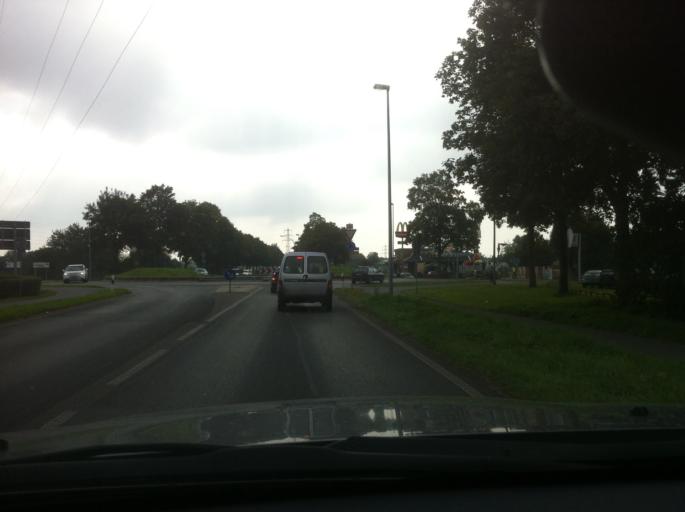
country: DE
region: North Rhine-Westphalia
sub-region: Regierungsbezirk Dusseldorf
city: Kleve
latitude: 51.7912
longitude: 6.1541
